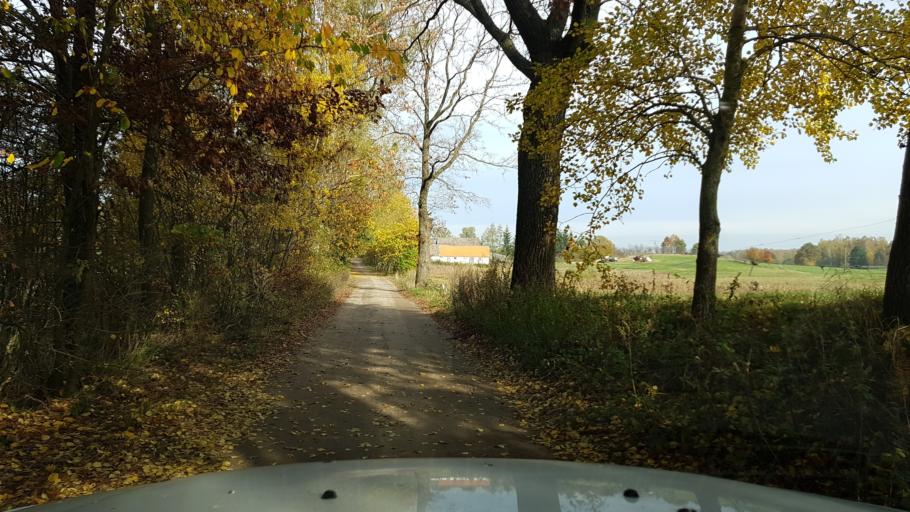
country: PL
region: West Pomeranian Voivodeship
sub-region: Powiat swidwinski
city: Polczyn-Zdroj
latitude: 53.7538
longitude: 16.0315
